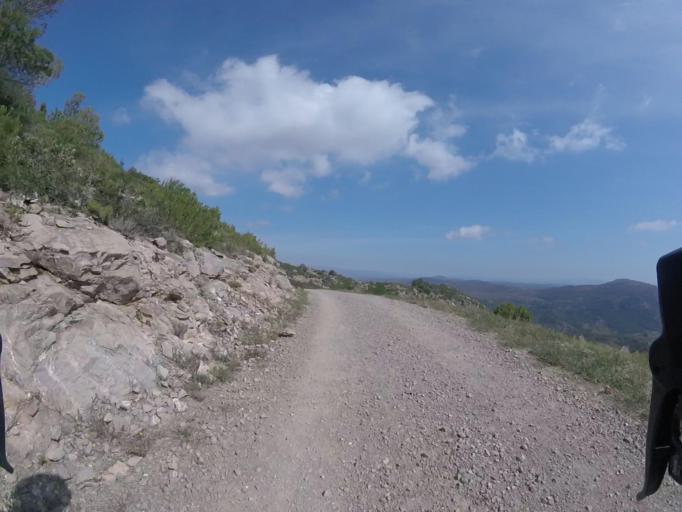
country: ES
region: Valencia
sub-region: Provincia de Castello
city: Benicassim
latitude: 40.0983
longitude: 0.0461
